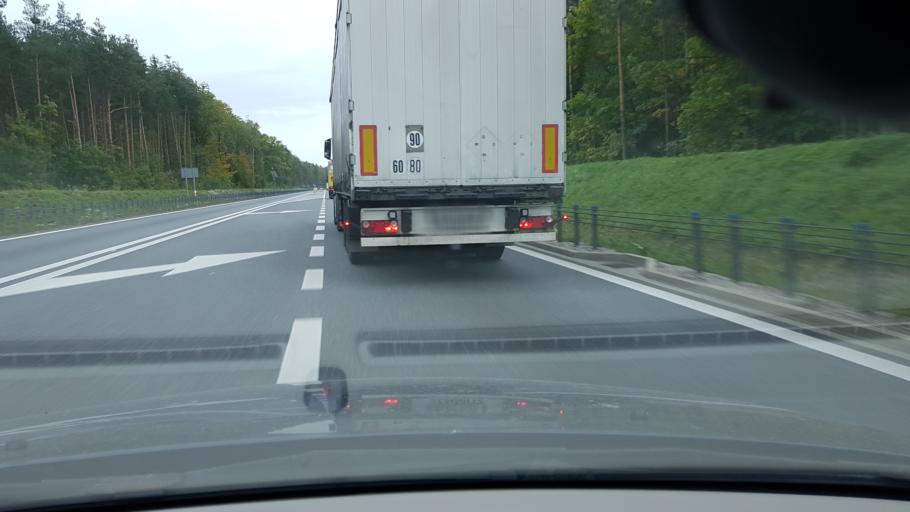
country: PL
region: Masovian Voivodeship
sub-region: Powiat zyrardowski
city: Wiskitki
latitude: 52.0643
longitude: 20.3905
